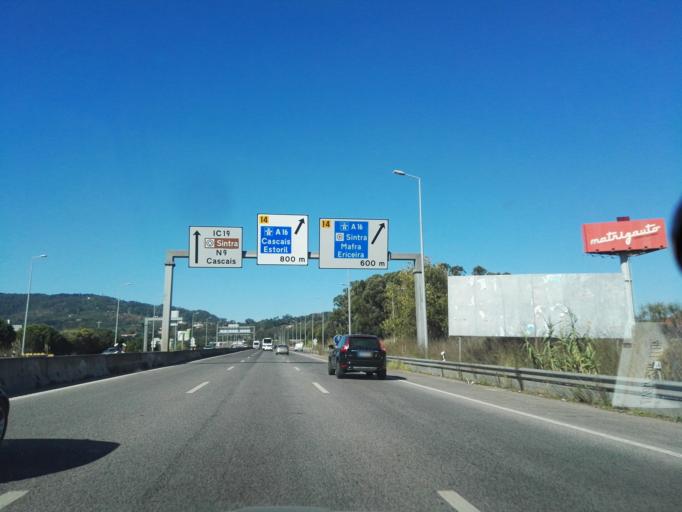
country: PT
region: Lisbon
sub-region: Sintra
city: Rio de Mouro
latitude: 38.7783
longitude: -9.3514
